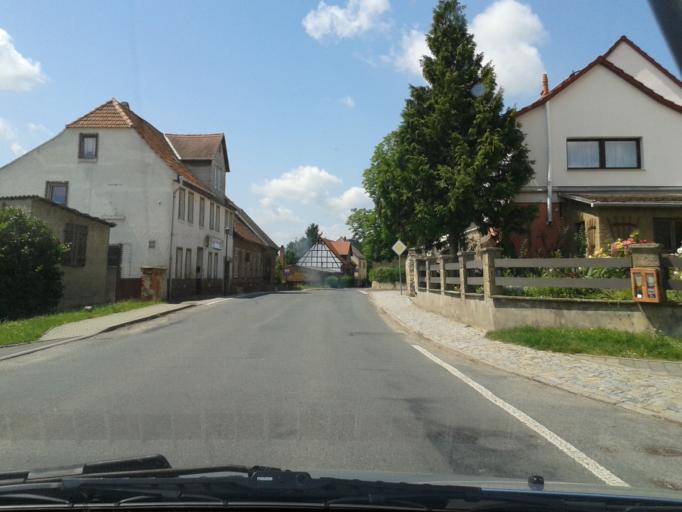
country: DE
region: Thuringia
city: Wichmar
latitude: 51.0438
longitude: 11.6634
